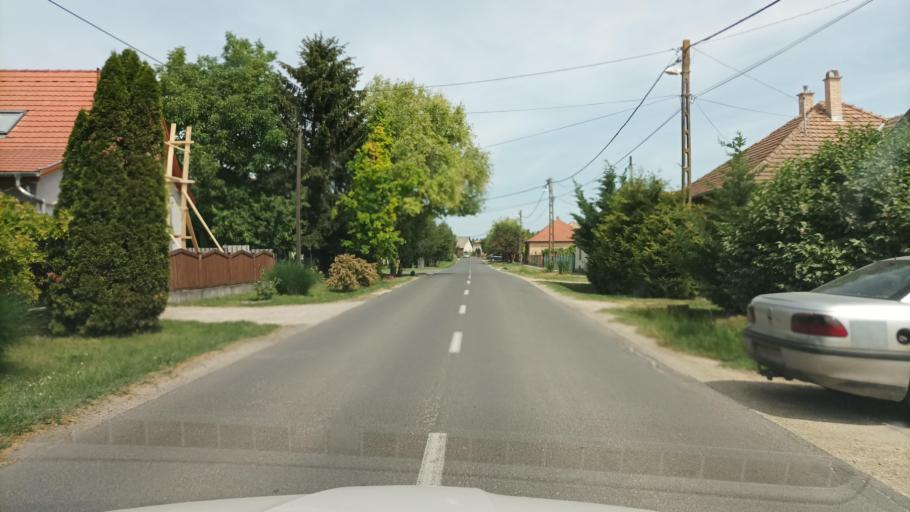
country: HU
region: Pest
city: Rackeve
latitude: 47.1240
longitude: 18.9468
